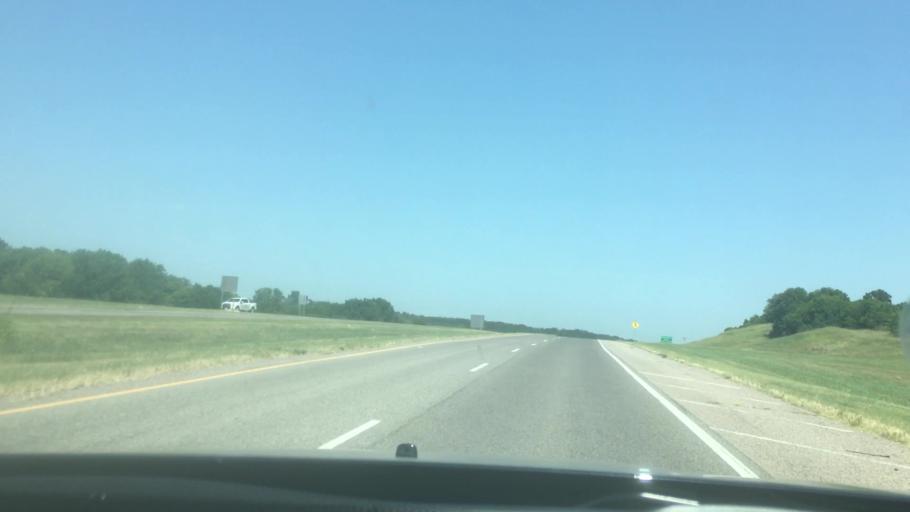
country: US
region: Oklahoma
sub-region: Pontotoc County
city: Ada
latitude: 34.7279
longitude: -96.6365
